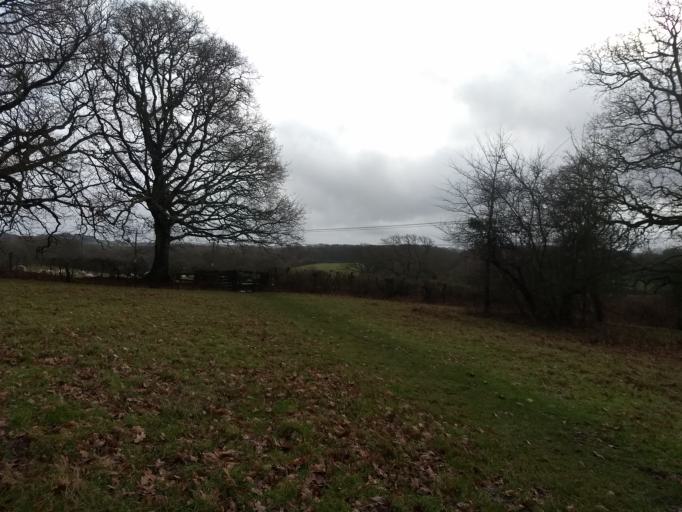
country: GB
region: England
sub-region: Isle of Wight
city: Newport
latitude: 50.7123
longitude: -1.2395
